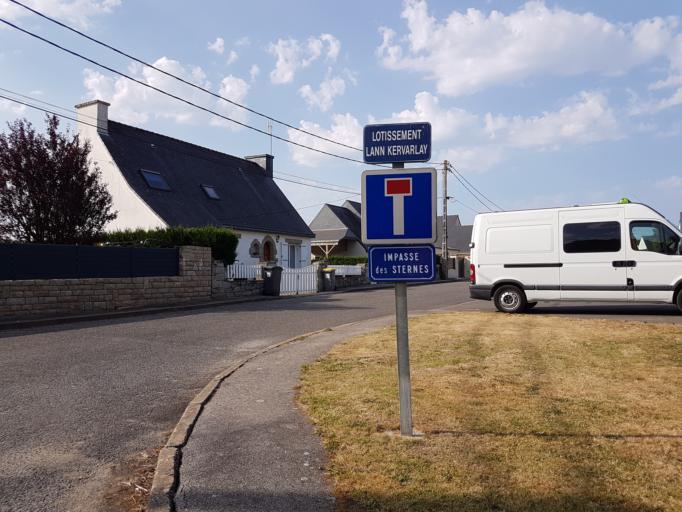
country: FR
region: Brittany
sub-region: Departement du Morbihan
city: Etel
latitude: 47.6829
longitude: -3.2063
